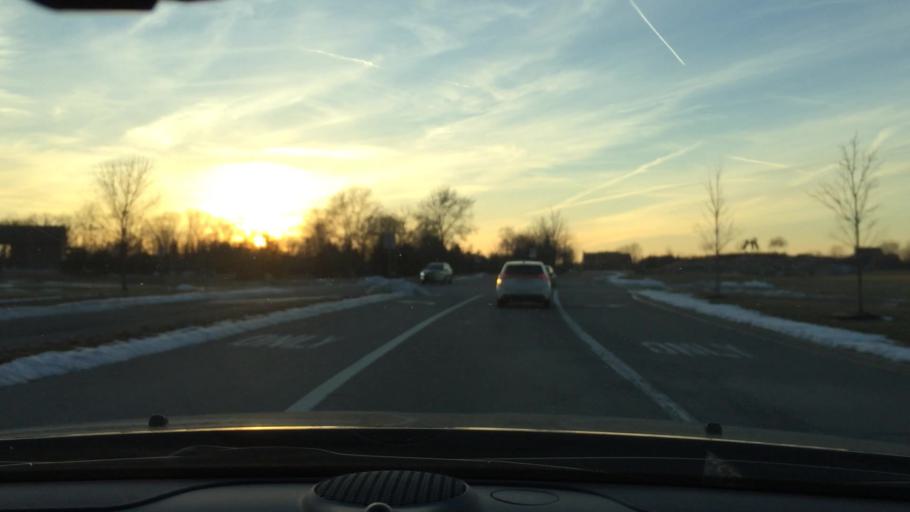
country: US
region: Ohio
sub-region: Franklin County
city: Dublin
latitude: 40.0863
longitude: -83.1605
